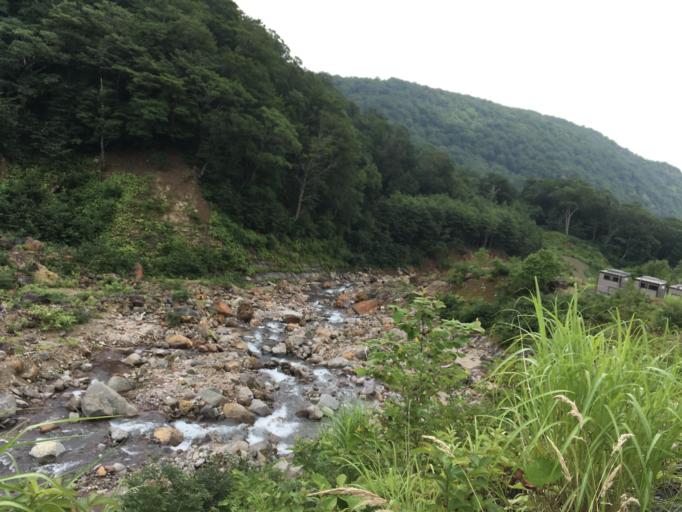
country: JP
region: Iwate
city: Ichinoseki
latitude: 38.9628
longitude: 140.8431
